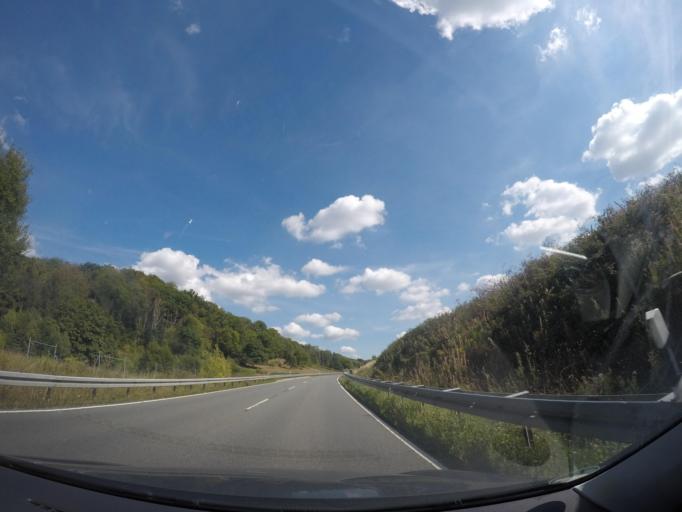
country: DE
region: Lower Saxony
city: Bad Lauterberg im Harz
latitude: 51.6248
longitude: 10.4417
